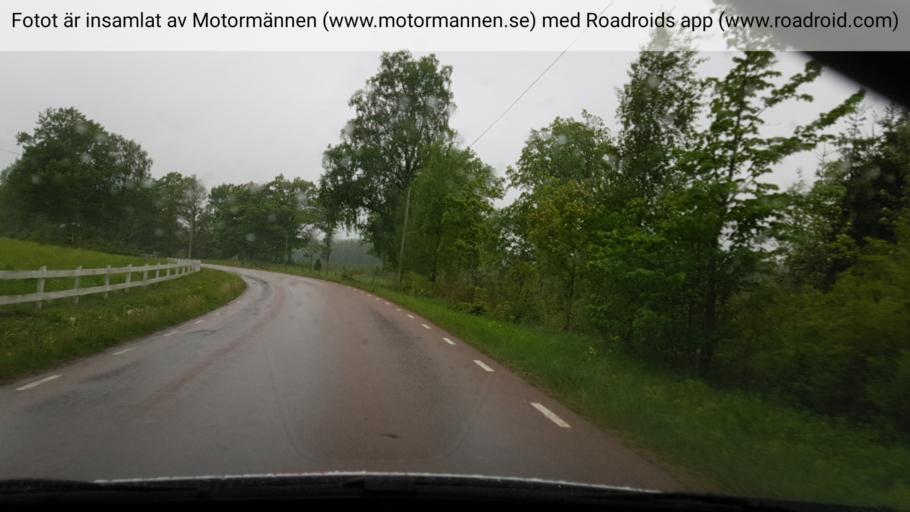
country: SE
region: Vaestra Goetaland
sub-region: Ulricehamns Kommun
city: Ulricehamn
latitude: 57.8329
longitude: 13.4751
